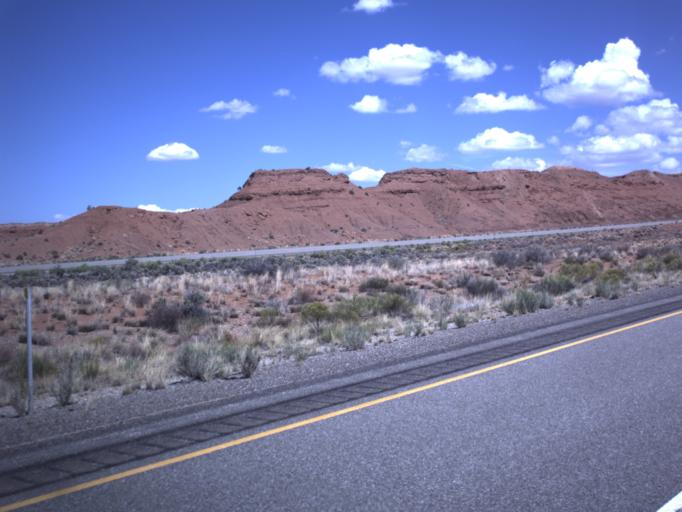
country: US
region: Utah
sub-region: Emery County
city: Ferron
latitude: 38.8466
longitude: -111.0338
